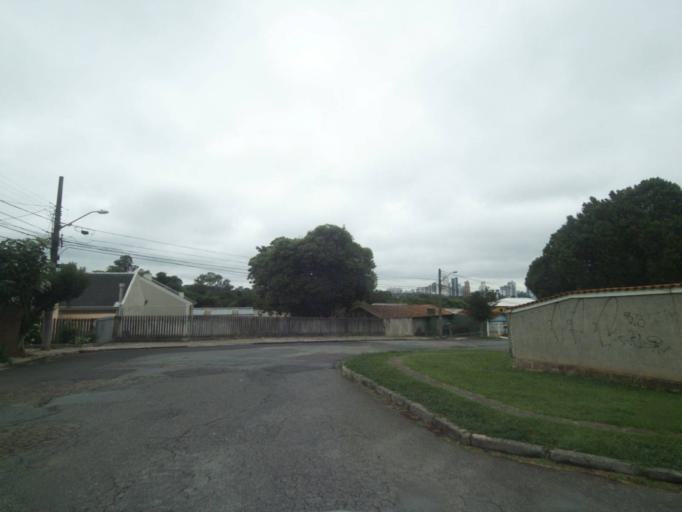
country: BR
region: Parana
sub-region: Curitiba
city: Curitiba
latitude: -25.4268
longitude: -49.3425
